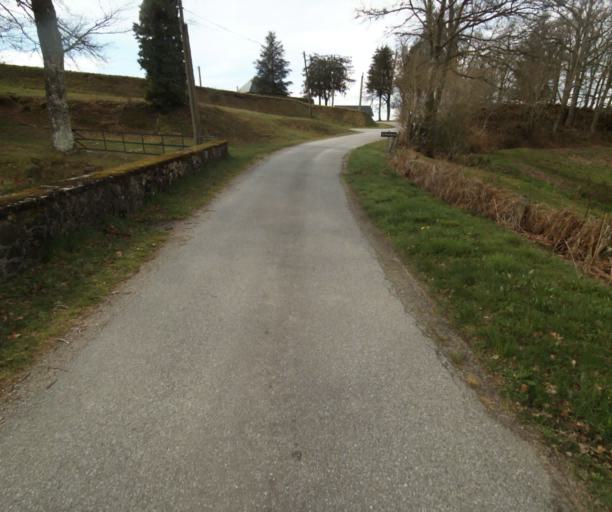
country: FR
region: Limousin
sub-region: Departement de la Correze
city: Correze
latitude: 45.3869
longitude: 1.8951
